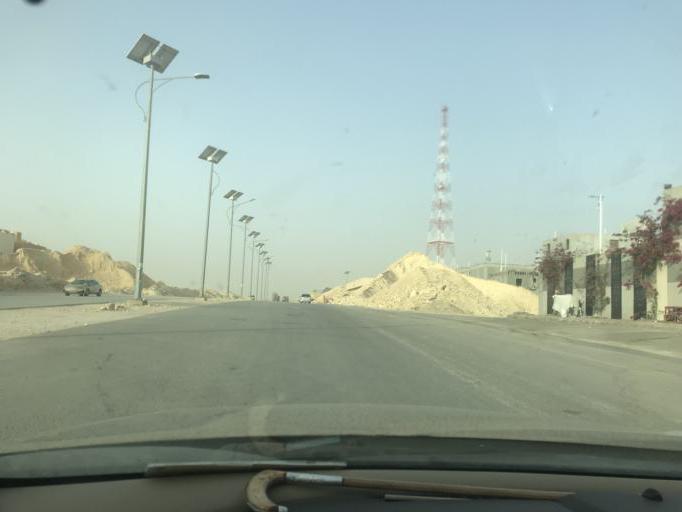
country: SA
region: Ar Riyad
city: Riyadh
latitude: 24.8393
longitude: 46.6699
